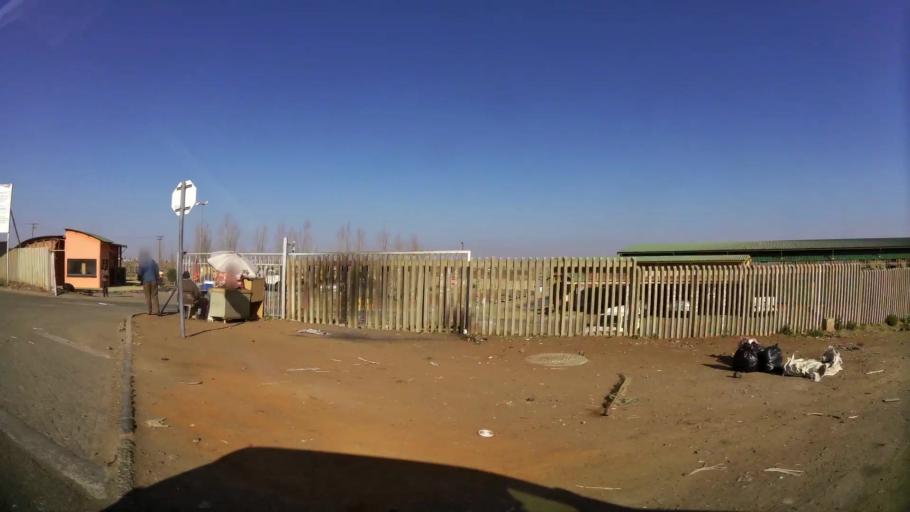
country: ZA
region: Orange Free State
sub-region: Mangaung Metropolitan Municipality
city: Bloemfontein
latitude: -29.1793
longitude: 26.1977
